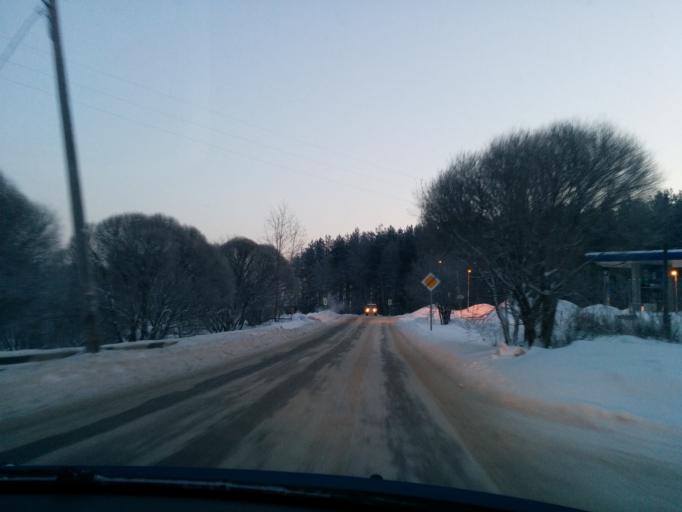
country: RU
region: Perm
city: Novyye Lyady
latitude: 58.0483
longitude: 56.5788
